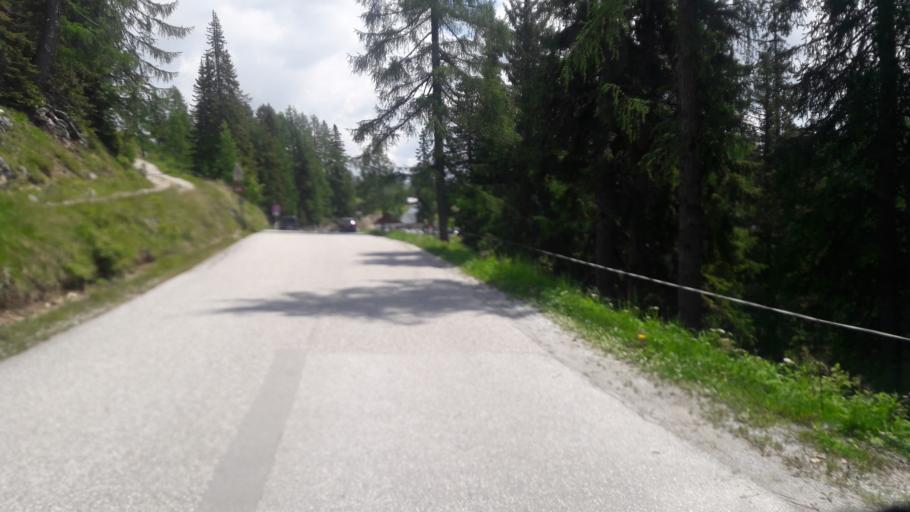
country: AT
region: Styria
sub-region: Politischer Bezirk Liezen
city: Tauplitz
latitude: 47.5934
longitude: 13.9830
